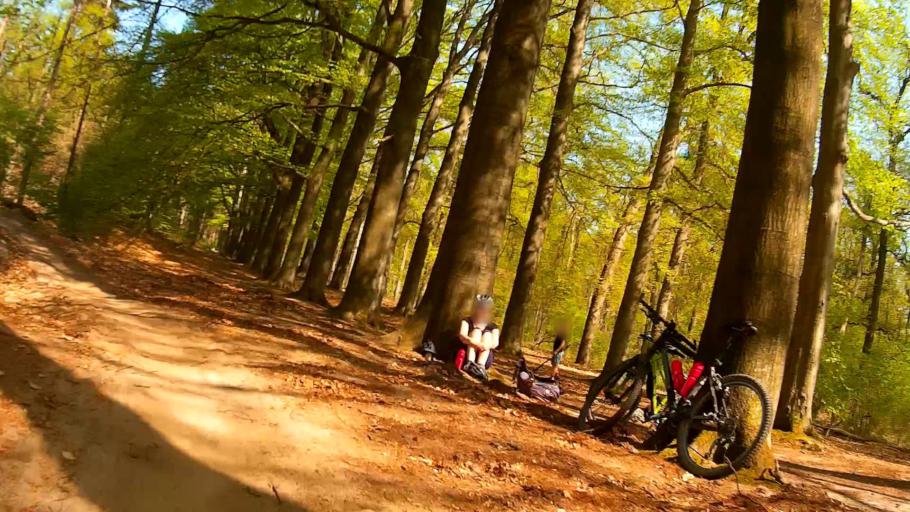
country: NL
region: Utrecht
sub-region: Gemeente Baarn
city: Baarn
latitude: 52.1922
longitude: 5.2543
